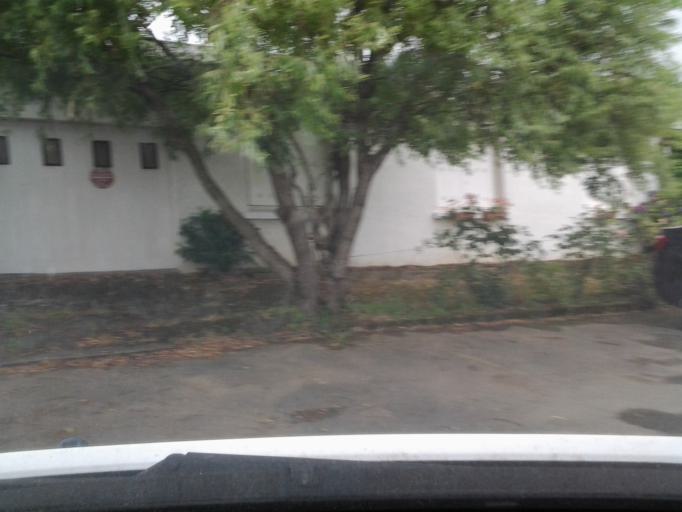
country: FR
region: Pays de la Loire
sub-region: Departement de la Vendee
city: La Roche-sur-Yon
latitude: 46.6838
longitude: -1.4313
